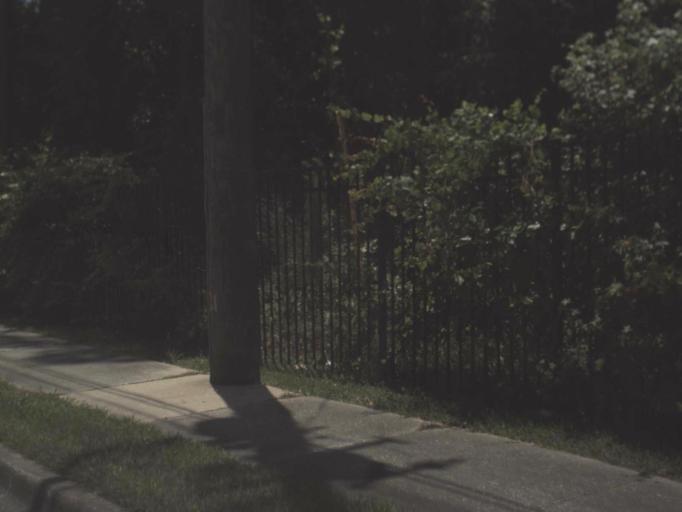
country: US
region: Florida
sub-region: Duval County
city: Jacksonville
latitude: 30.2904
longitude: -81.6192
